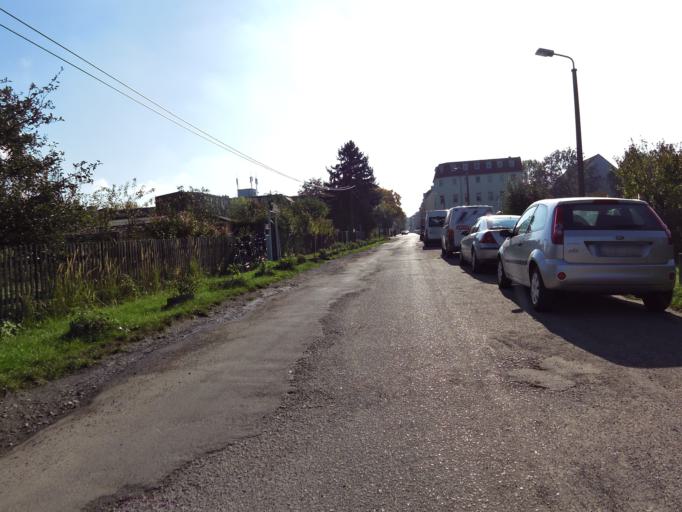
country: DE
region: Saxony
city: Leipzig
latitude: 51.3421
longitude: 12.3355
